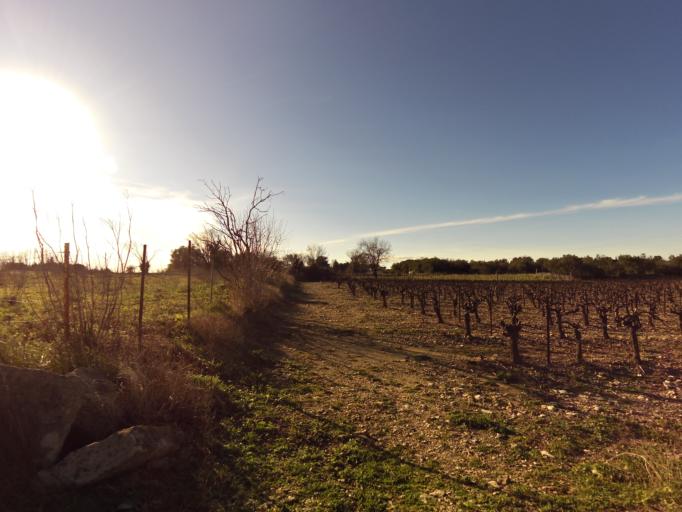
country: FR
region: Languedoc-Roussillon
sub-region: Departement du Gard
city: Aigues-Vives
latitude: 43.7454
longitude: 4.1777
